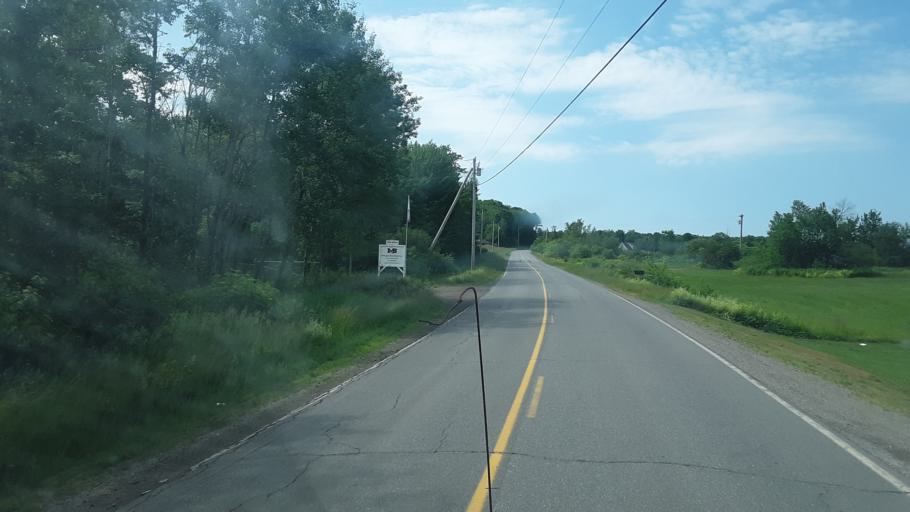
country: US
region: Maine
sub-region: Waldo County
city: Frankfort
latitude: 44.5929
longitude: -68.9436
